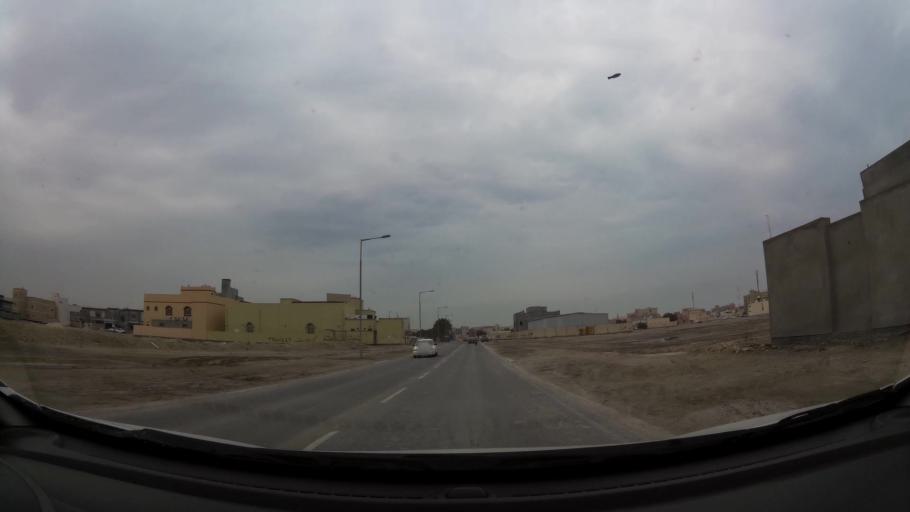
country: BH
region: Northern
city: Sitrah
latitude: 26.1649
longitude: 50.6235
